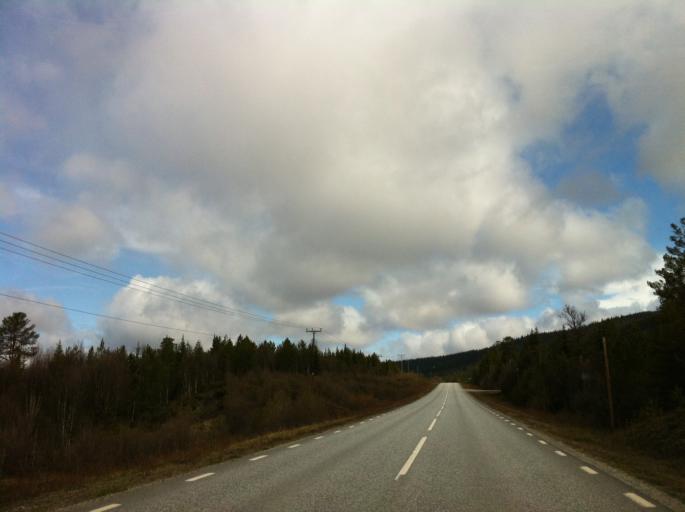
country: SE
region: Jaemtland
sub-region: Are Kommun
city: Are
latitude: 62.5599
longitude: 12.5669
